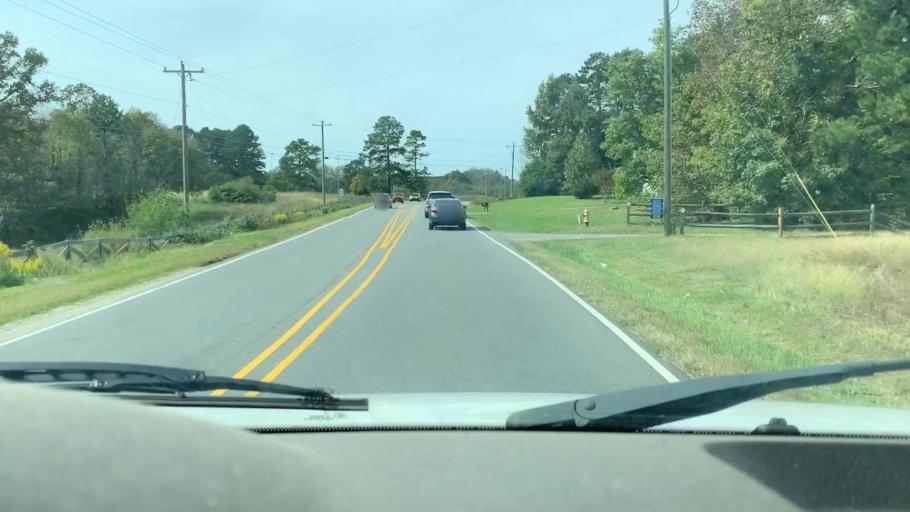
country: US
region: North Carolina
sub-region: Mecklenburg County
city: Huntersville
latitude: 35.4463
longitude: -80.7838
